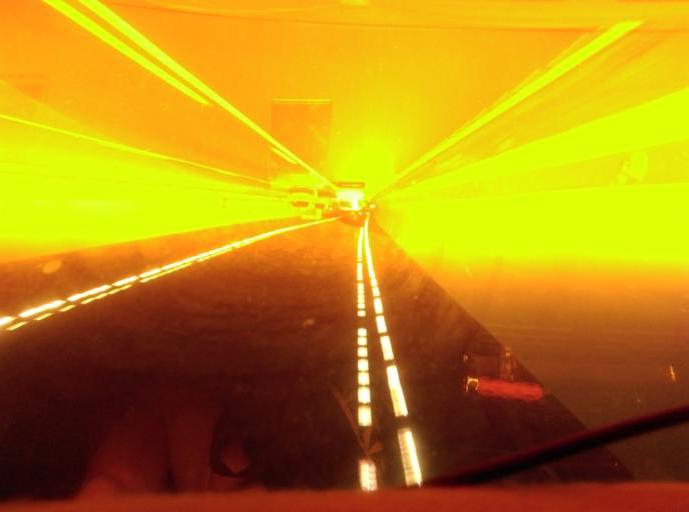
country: TW
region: Taipei
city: Taipei
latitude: 24.9708
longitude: 121.5512
